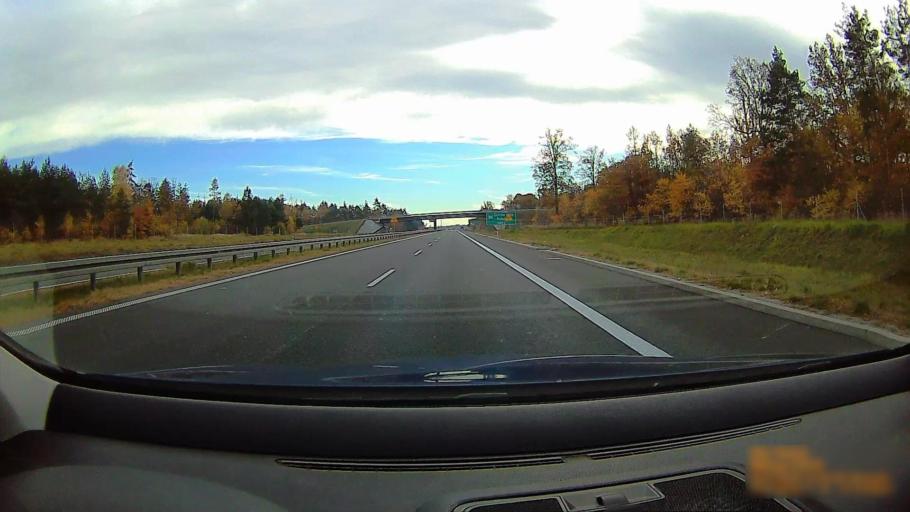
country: PL
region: Greater Poland Voivodeship
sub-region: Powiat ostrowski
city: Ostrow Wielkopolski
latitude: 51.6569
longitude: 17.8641
